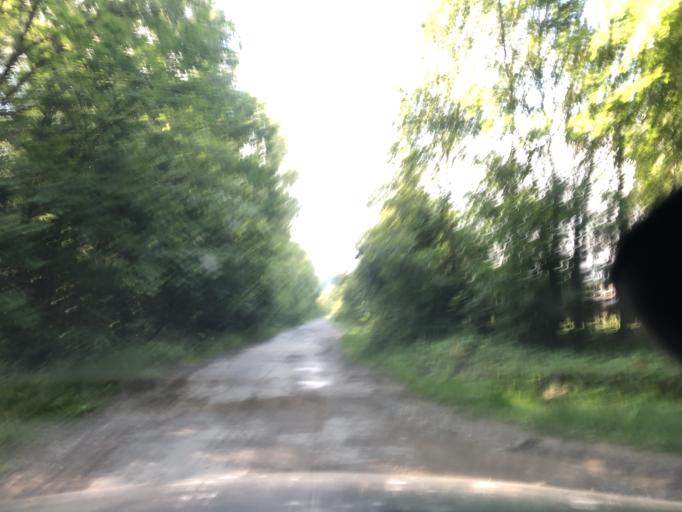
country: RU
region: Tula
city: Shvartsevskiy
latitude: 54.2546
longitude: 37.9246
